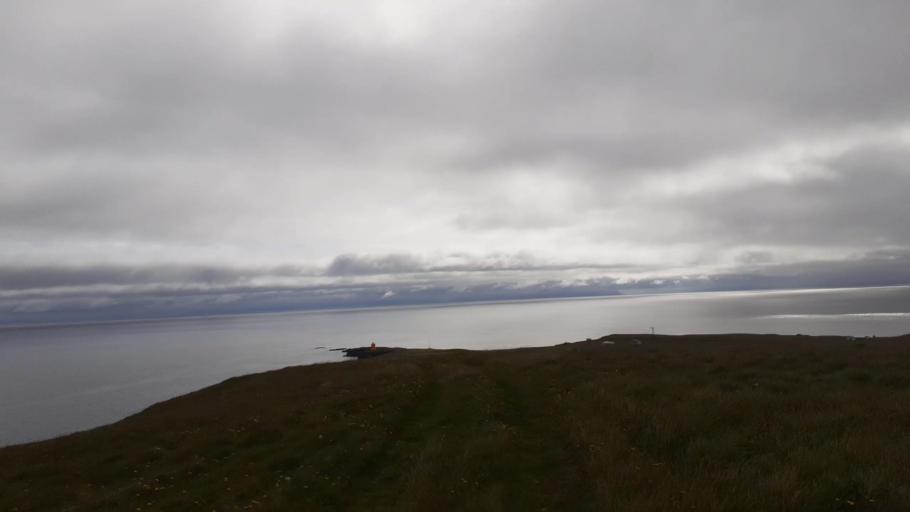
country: IS
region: Northeast
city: Dalvik
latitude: 66.5360
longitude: -17.9818
